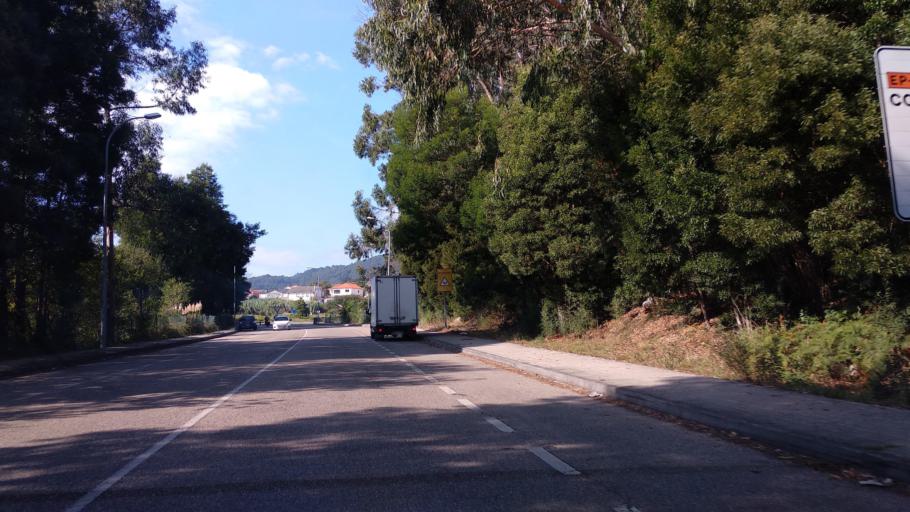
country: ES
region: Galicia
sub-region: Provincia de Pontevedra
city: Cangas
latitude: 42.2665
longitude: -8.7658
